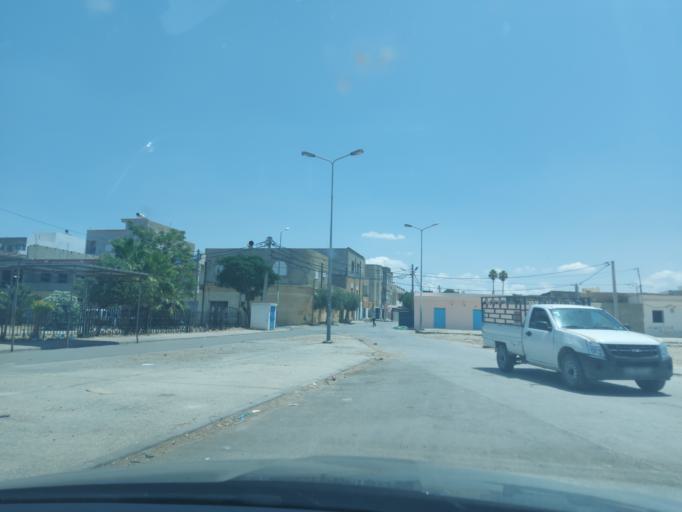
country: TN
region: Silyanah
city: Siliana
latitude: 36.0885
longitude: 9.3668
